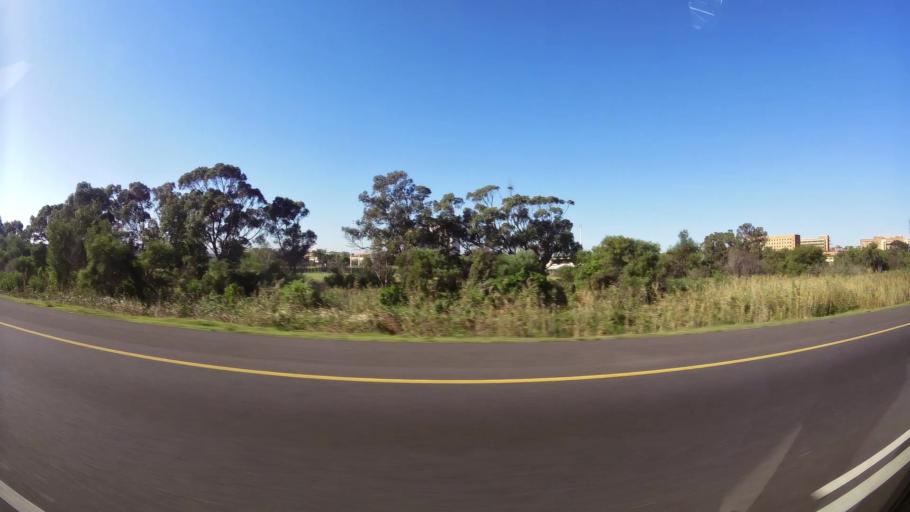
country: ZA
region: Eastern Cape
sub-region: Nelson Mandela Bay Metropolitan Municipality
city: Port Elizabeth
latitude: -33.9201
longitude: 25.5712
